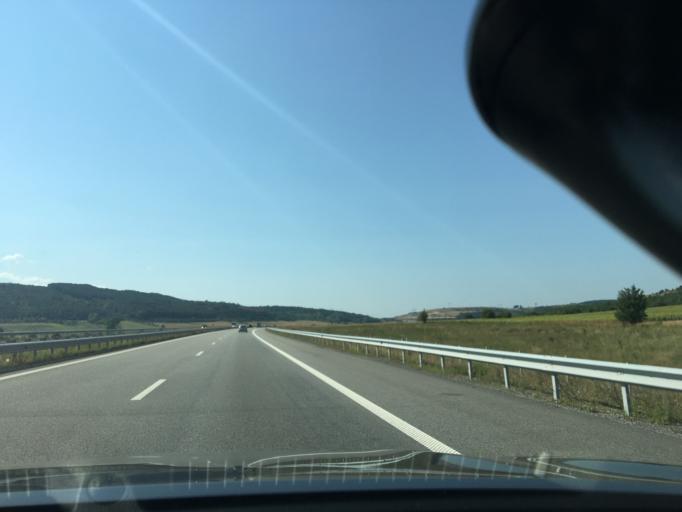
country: BG
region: Kyustendil
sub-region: Obshtina Bobovdol
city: Bobovdol
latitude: 42.4006
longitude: 23.1206
